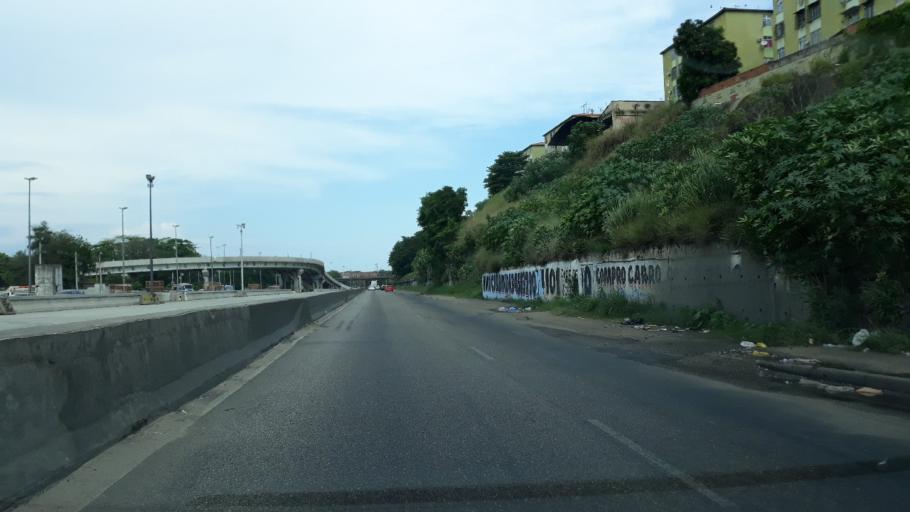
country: BR
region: Rio de Janeiro
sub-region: Duque De Caxias
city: Duque de Caxias
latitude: -22.8149
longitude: -43.2930
